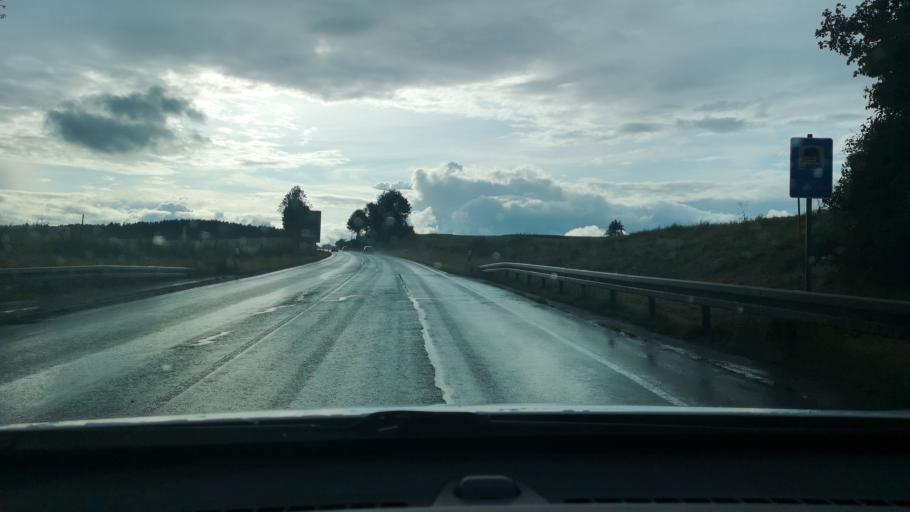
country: DE
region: Baden-Wuerttemberg
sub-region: Freiburg Region
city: Rottweil
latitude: 48.1490
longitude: 8.6262
